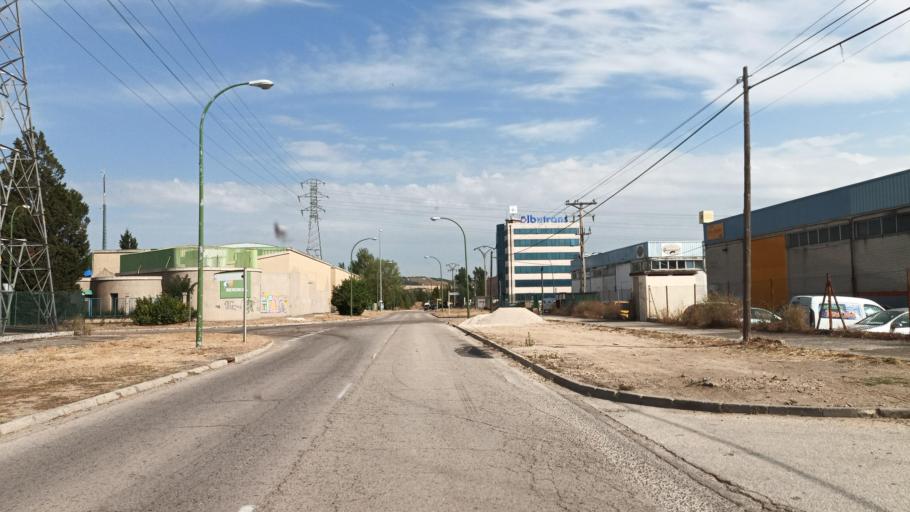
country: ES
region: Castille and Leon
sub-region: Provincia de Burgos
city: Burgos
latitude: 42.3616
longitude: -3.6469
